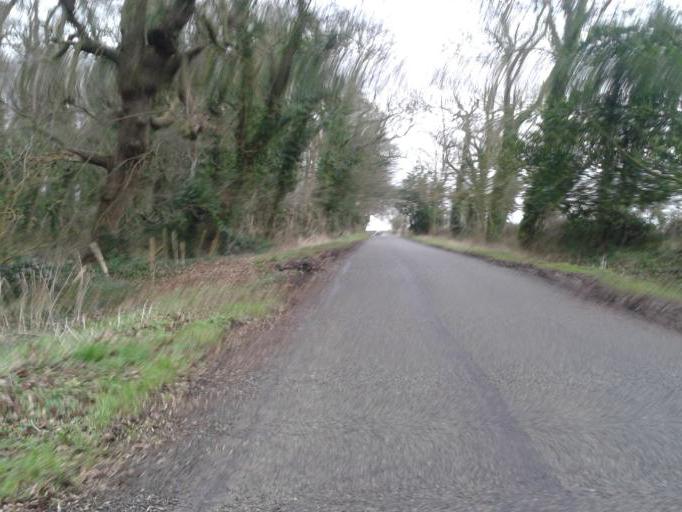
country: GB
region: England
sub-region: Warwickshire
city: Atherstone
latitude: 52.6347
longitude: -1.5499
